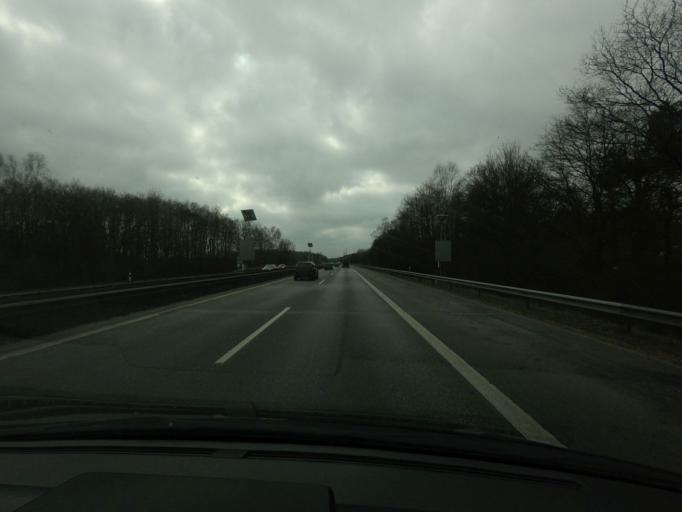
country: DE
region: Schleswig-Holstein
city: Ellerau
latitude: 53.7337
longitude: 9.9429
